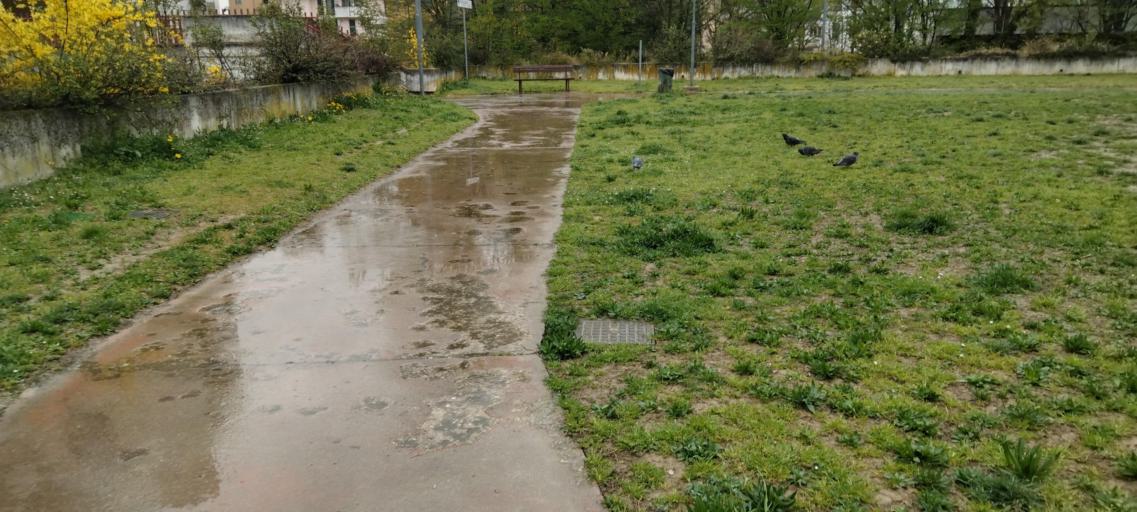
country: IT
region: Veneto
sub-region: Provincia di Vicenza
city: Vicenza
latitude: 45.5515
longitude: 11.5328
